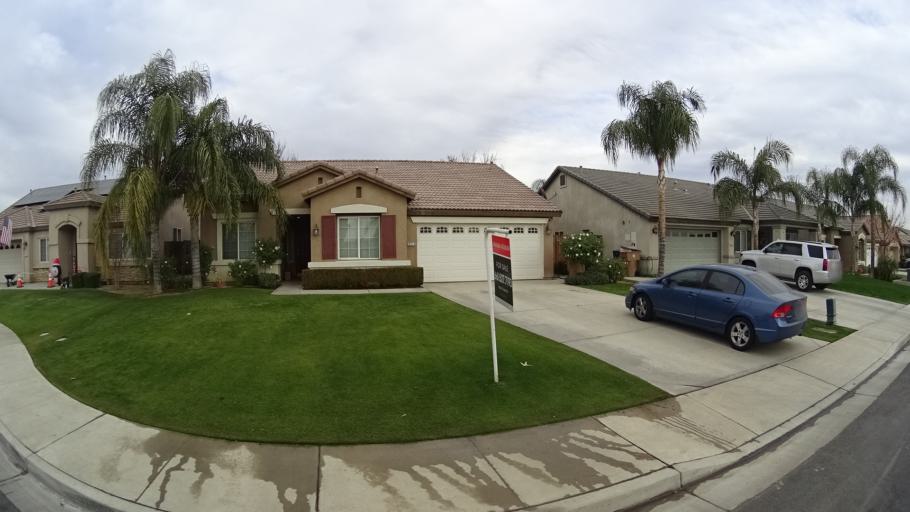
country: US
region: California
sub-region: Kern County
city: Rosedale
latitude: 35.4078
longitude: -119.1521
